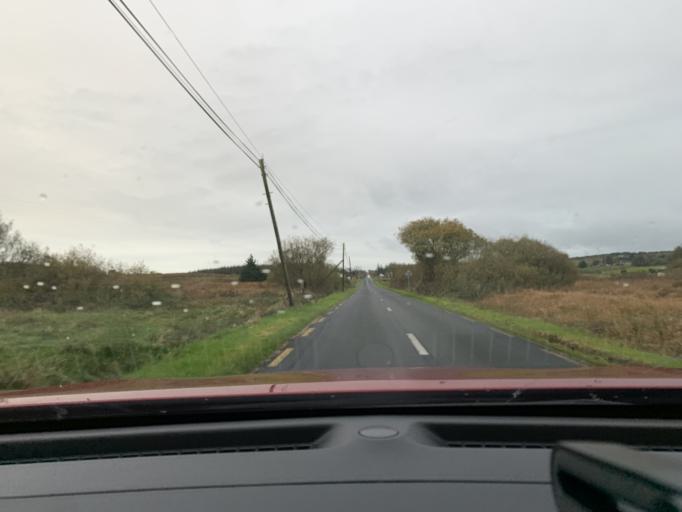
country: IE
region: Connaught
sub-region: Roscommon
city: Ballaghaderreen
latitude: 53.9687
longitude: -8.5389
